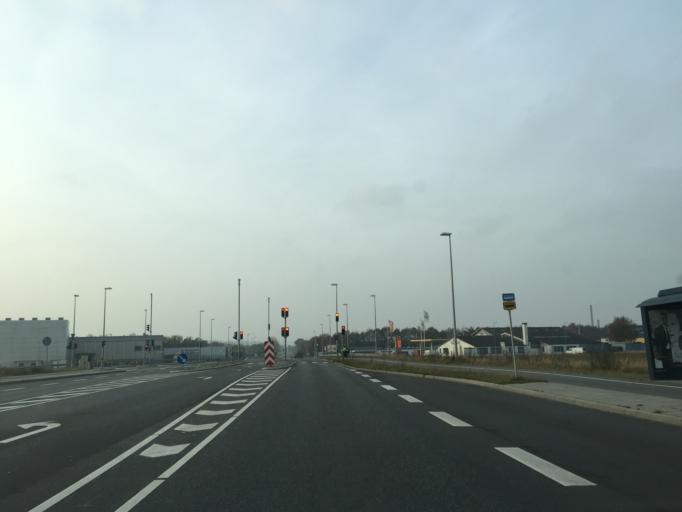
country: DK
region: Central Jutland
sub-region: Silkeborg Kommune
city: Silkeborg
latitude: 56.1878
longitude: 9.5753
